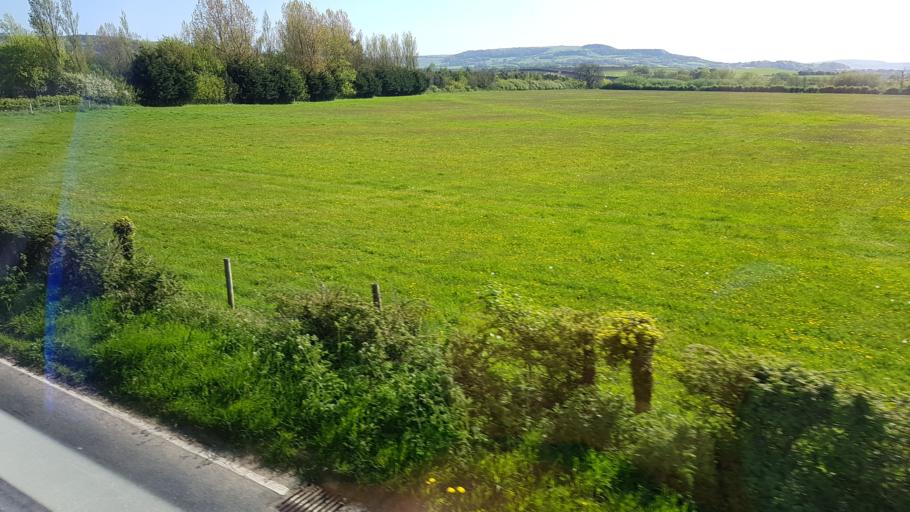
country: GB
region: England
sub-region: Isle of Wight
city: Newchurch
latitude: 50.6516
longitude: -1.2188
